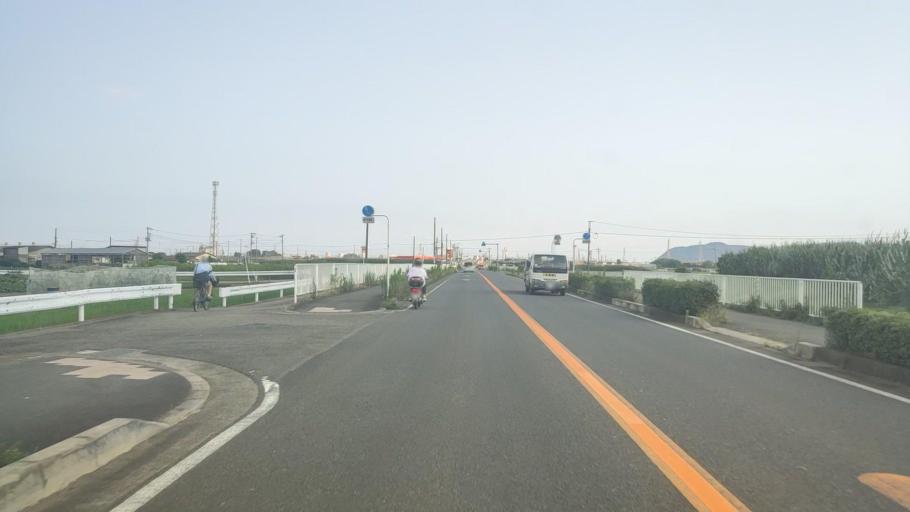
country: JP
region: Kanagawa
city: Isehara
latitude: 35.3676
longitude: 139.3227
